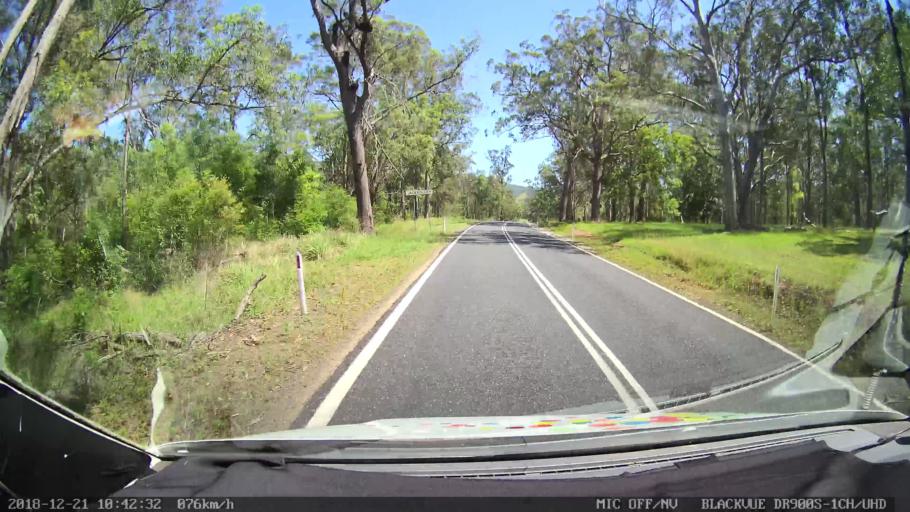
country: AU
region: New South Wales
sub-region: Clarence Valley
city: Gordon
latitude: -29.5847
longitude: 152.5618
